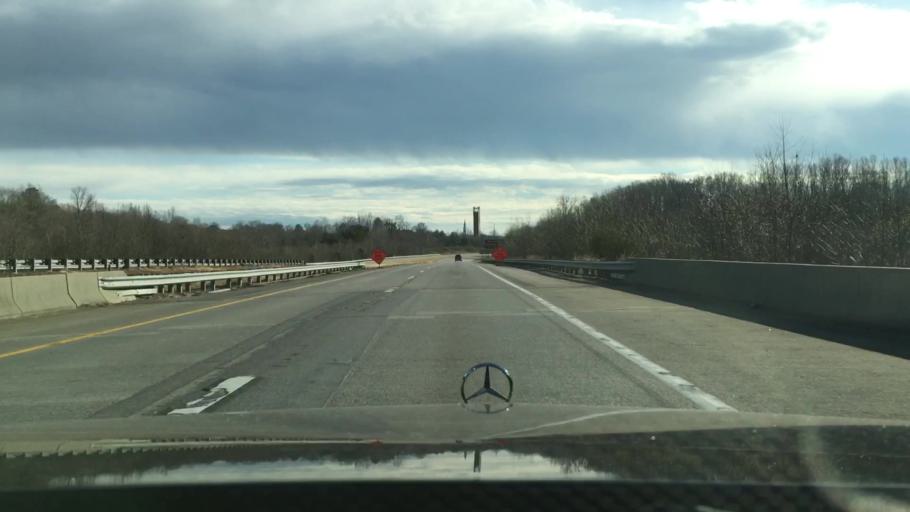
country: US
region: Virginia
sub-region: City of Danville
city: Danville
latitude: 36.5950
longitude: -79.3571
